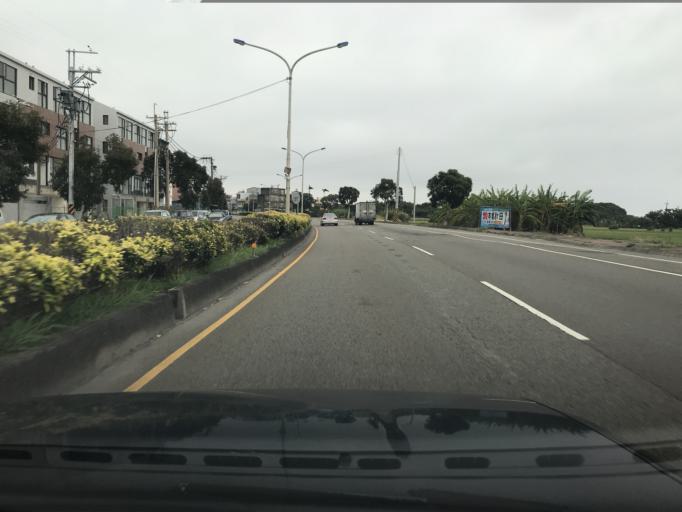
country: TW
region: Taiwan
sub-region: Hsinchu
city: Hsinchu
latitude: 24.8304
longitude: 120.9266
